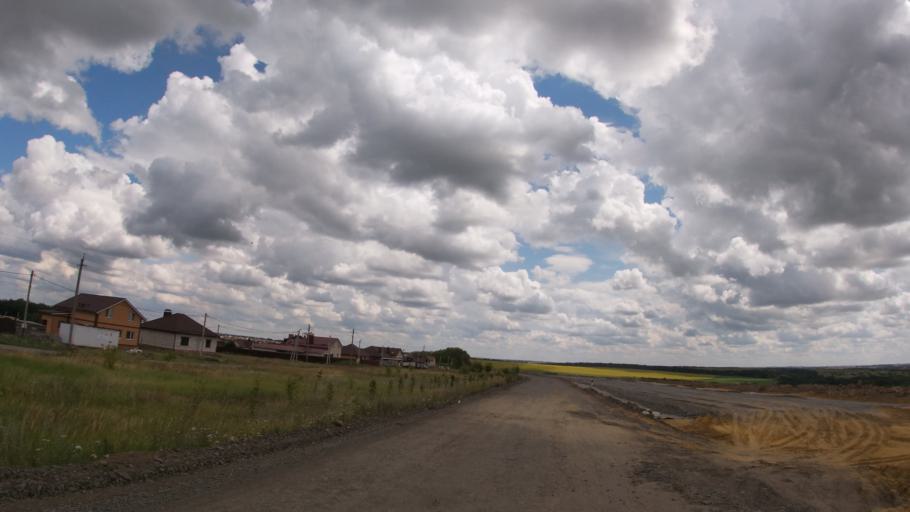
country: RU
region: Belgorod
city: Mayskiy
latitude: 50.5015
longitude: 36.4474
